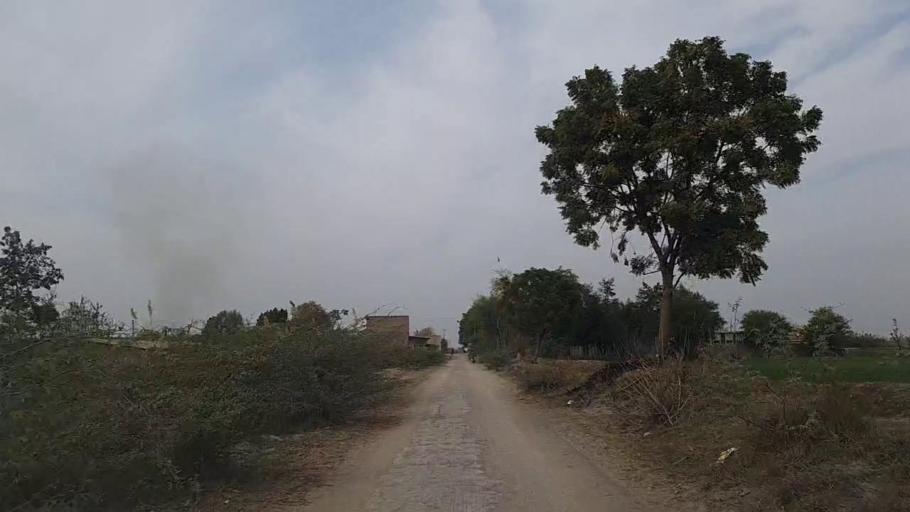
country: PK
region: Sindh
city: Daur
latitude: 26.4471
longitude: 68.4519
